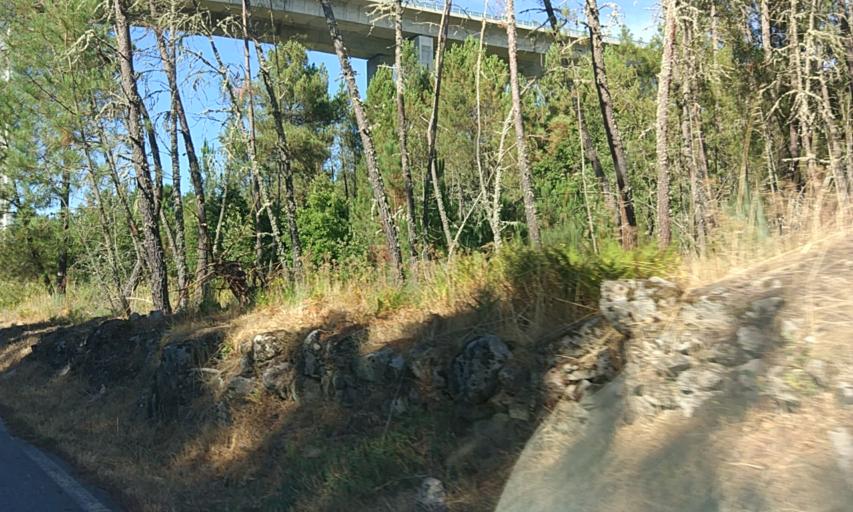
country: PT
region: Vila Real
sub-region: Sabrosa
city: Sabrosa
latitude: 41.3586
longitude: -7.5732
